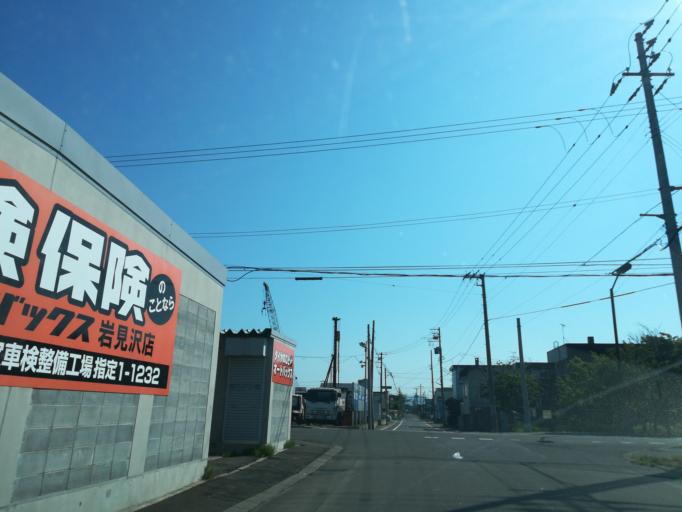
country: JP
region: Hokkaido
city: Iwamizawa
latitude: 43.1886
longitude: 141.7389
